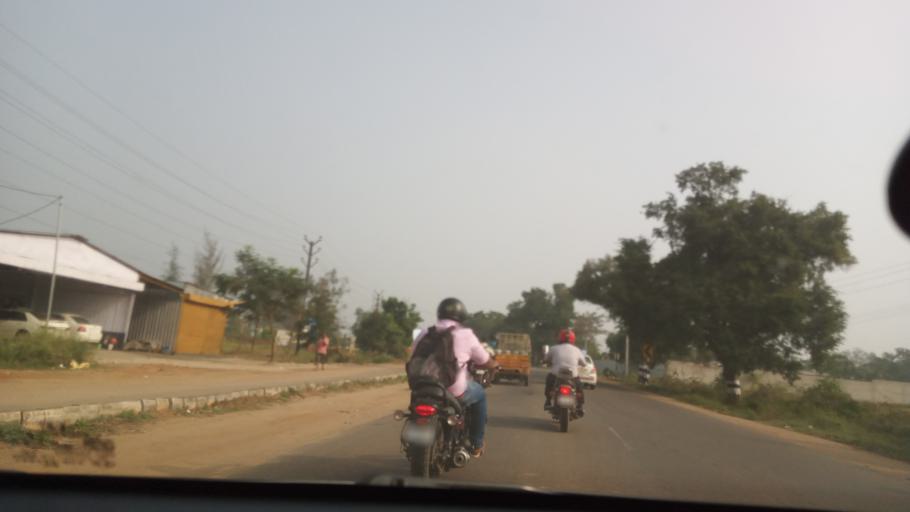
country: IN
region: Tamil Nadu
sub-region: Coimbatore
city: Annur
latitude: 11.1619
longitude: 77.0516
